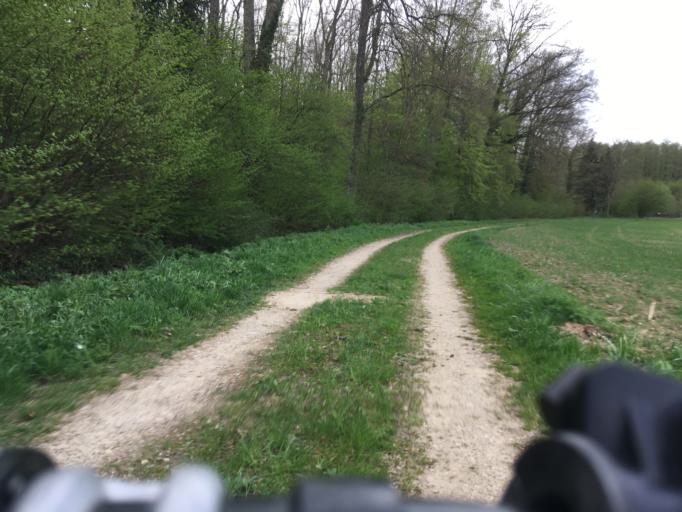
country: DE
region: Baden-Wuerttemberg
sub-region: Freiburg Region
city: Gailingen
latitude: 47.7110
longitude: 8.7482
